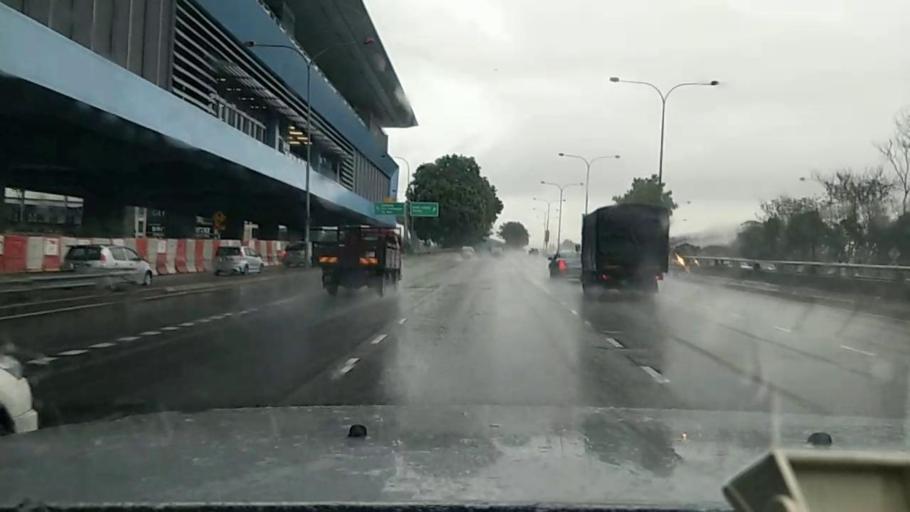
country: MY
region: Selangor
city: Kampong Baharu Balakong
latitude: 3.0406
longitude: 101.7734
